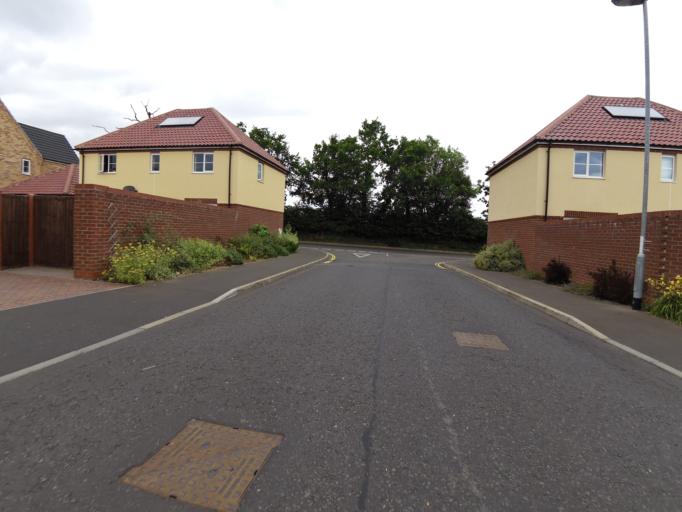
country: GB
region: England
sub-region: Norfolk
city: Diss
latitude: 52.3782
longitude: 1.1256
